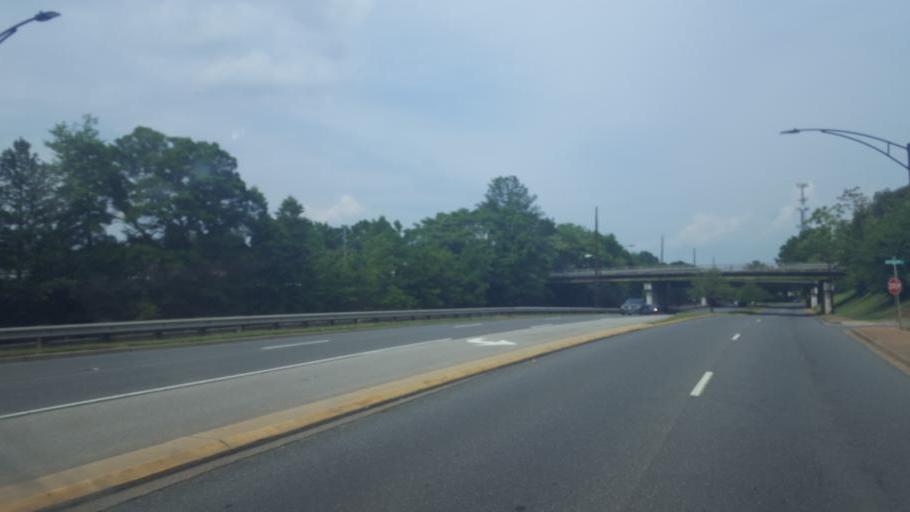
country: US
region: South Carolina
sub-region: York County
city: Rock Hill
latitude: 34.9287
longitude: -81.0247
